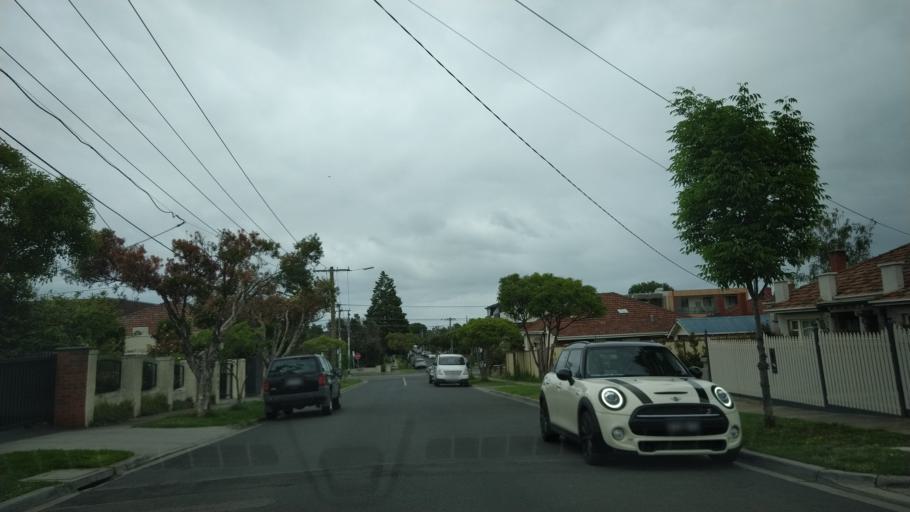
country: AU
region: Victoria
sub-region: Glen Eira
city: Caulfield
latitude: -37.8869
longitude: 145.0278
